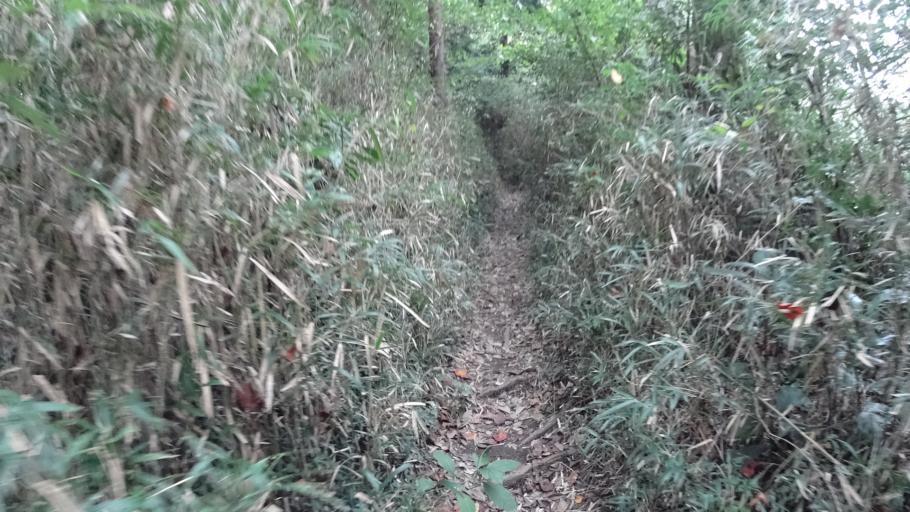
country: JP
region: Kanagawa
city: Zushi
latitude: 35.3020
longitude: 139.6187
